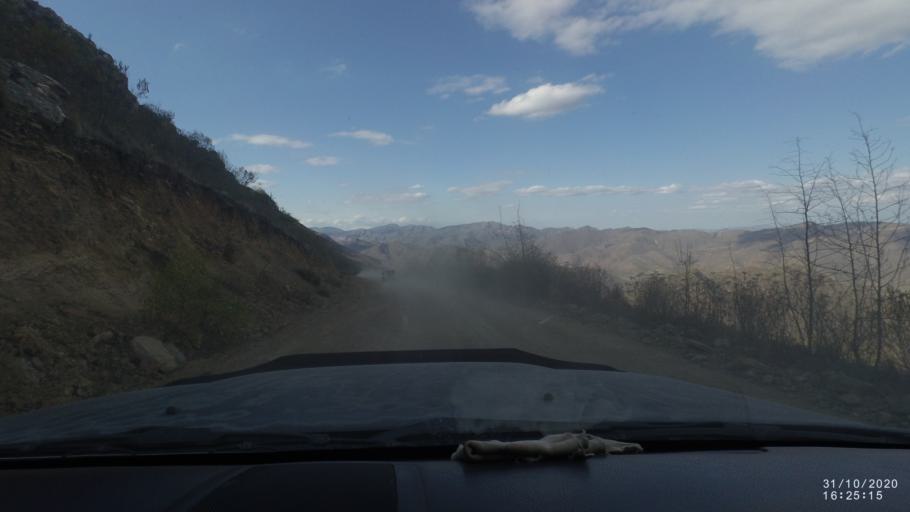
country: BO
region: Chuquisaca
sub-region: Provincia Zudanez
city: Mojocoya
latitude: -18.4021
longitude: -64.5874
